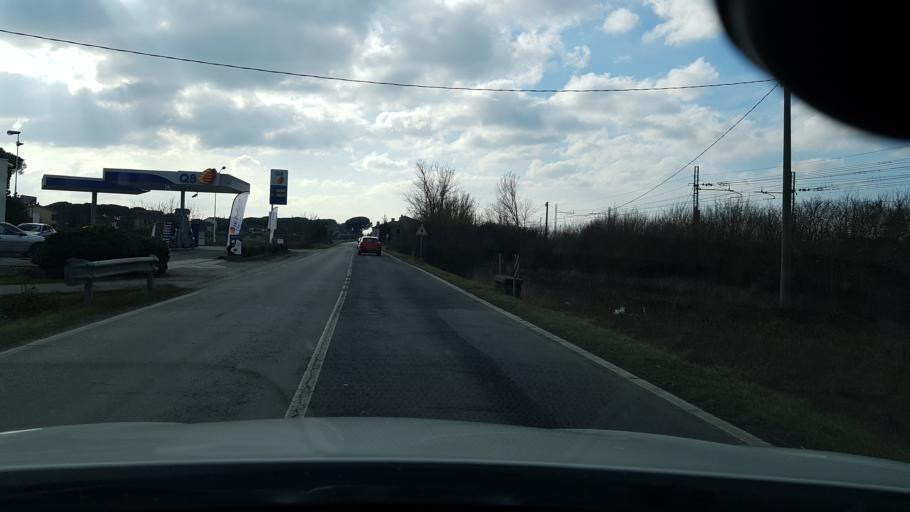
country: IT
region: Tuscany
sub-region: Province of Arezzo
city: Terontola
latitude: 43.1847
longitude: 12.0134
